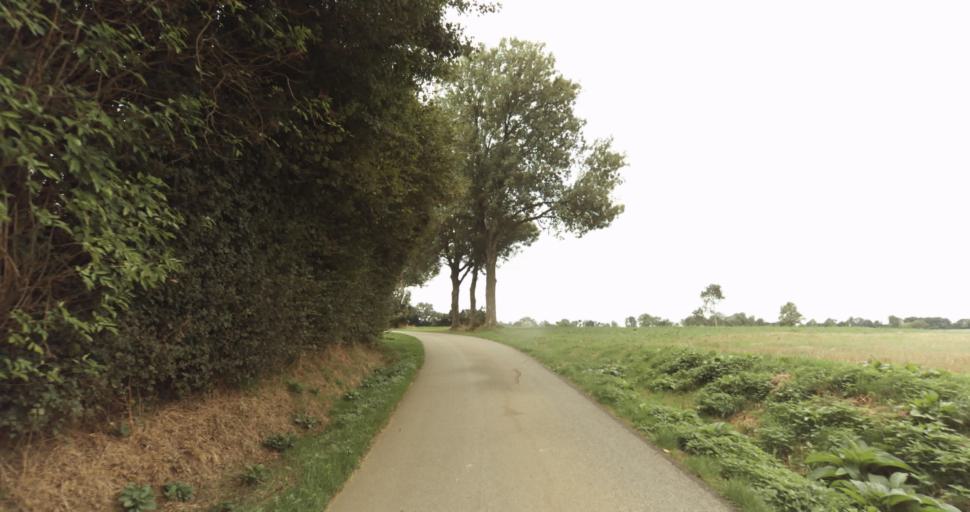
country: FR
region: Lower Normandy
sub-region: Departement de l'Orne
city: Gace
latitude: 48.7394
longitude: 0.3349
